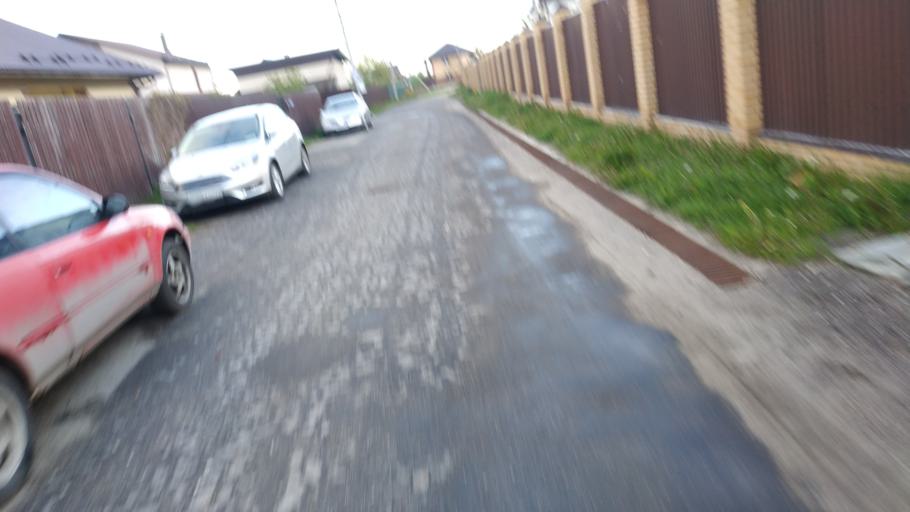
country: RU
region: Moskovskaya
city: Ramenskoye
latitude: 55.5849
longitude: 38.2941
